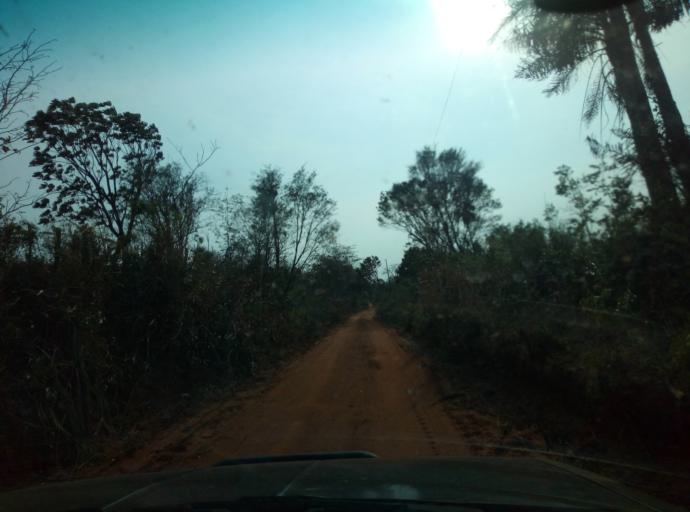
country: PY
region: Caaguazu
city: San Joaquin
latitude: -25.1512
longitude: -56.1036
